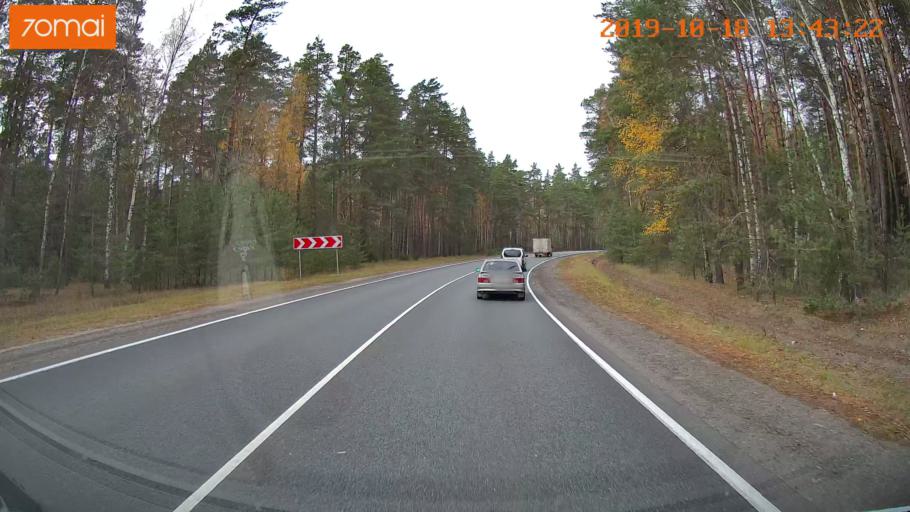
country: RU
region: Rjazan
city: Solotcha
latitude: 54.9298
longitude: 39.9755
